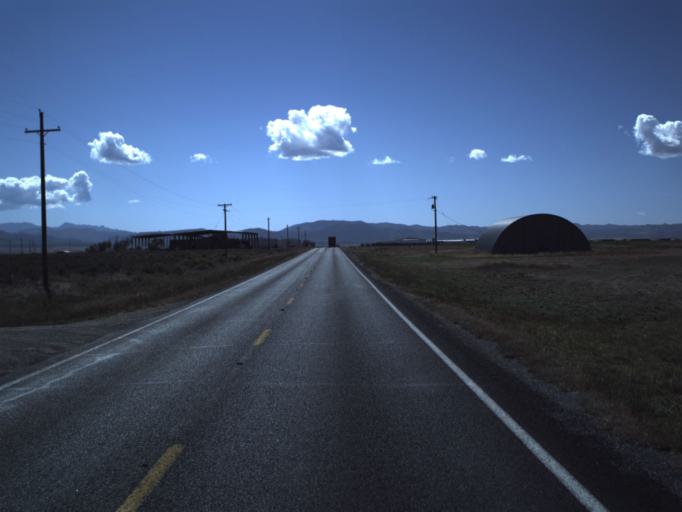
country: US
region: Utah
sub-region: Washington County
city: Enterprise
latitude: 37.6902
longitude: -113.6565
